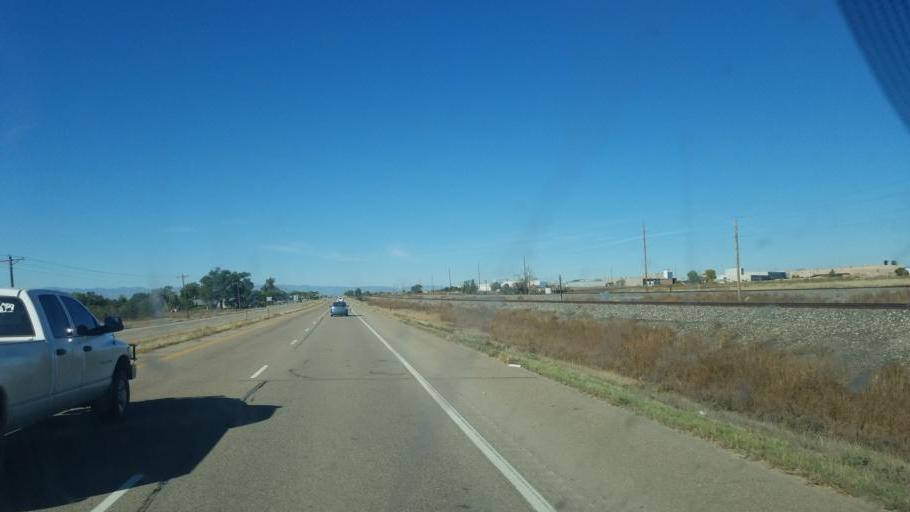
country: US
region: Colorado
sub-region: Pueblo County
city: Pueblo
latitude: 38.2759
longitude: -104.4740
